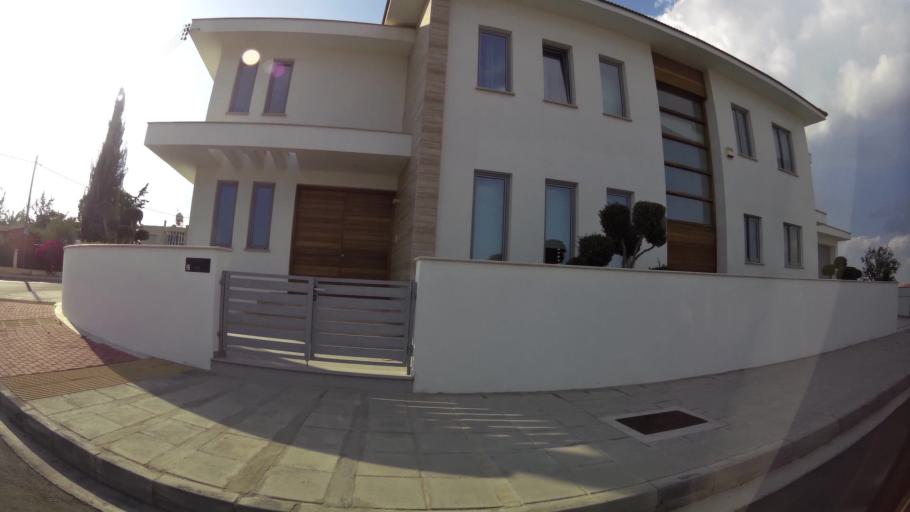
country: CY
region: Larnaka
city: Dhromolaxia
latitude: 34.8816
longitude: 33.5866
